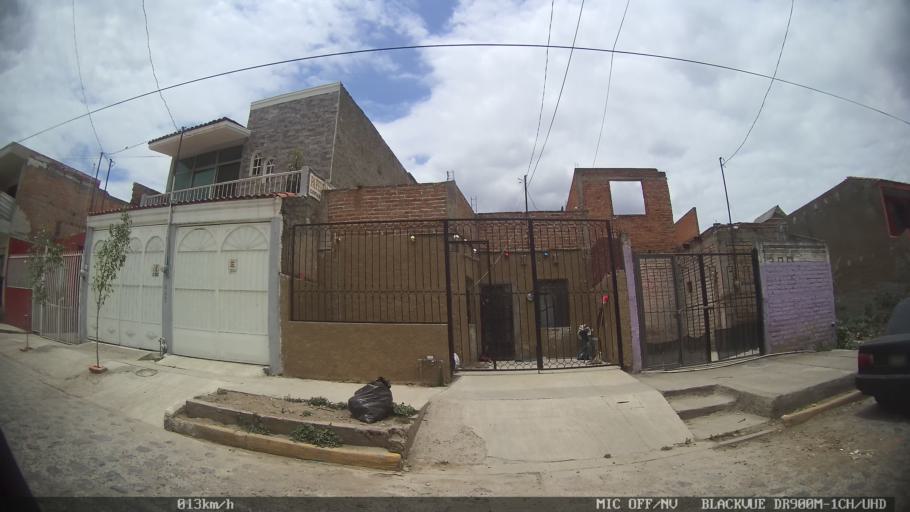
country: MX
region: Jalisco
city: Tonala
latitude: 20.6474
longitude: -103.2581
